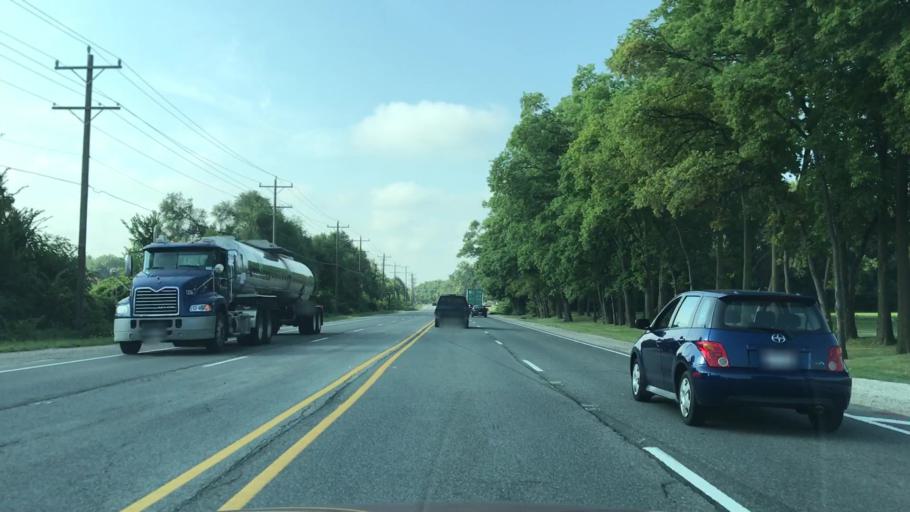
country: US
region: Illinois
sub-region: Will County
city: Lockport
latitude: 41.6087
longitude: -88.0752
